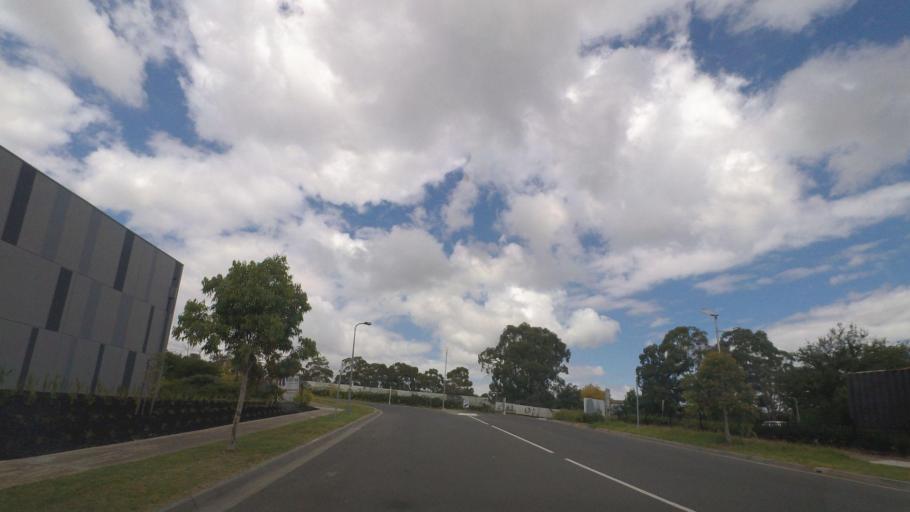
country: AU
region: Victoria
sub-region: Knox
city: Scoresby
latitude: -37.9143
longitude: 145.2344
